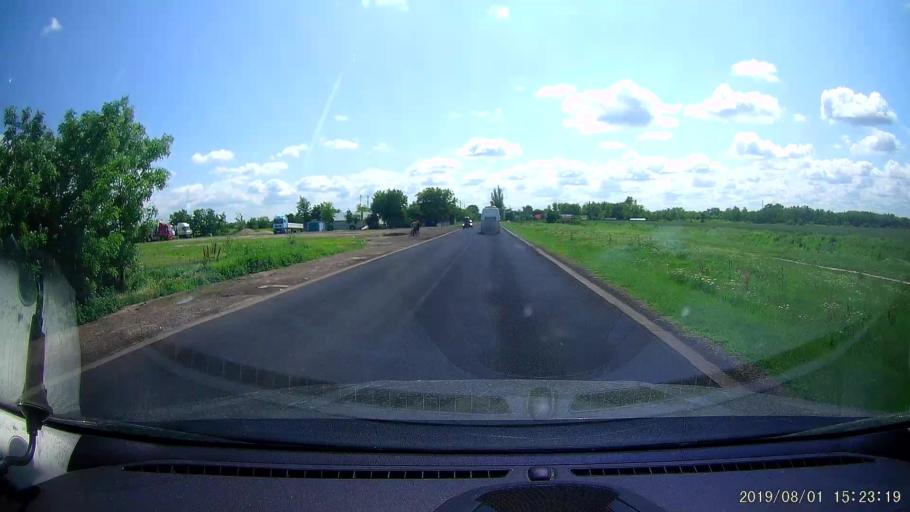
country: RO
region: Braila
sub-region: Comuna Viziru
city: Lanurile
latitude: 45.0424
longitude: 27.7617
